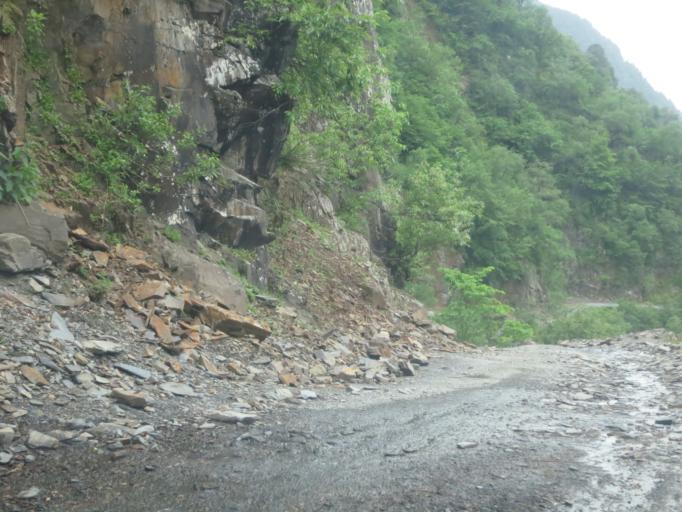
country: GE
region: Kakheti
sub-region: Telavi
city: Telavi
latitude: 42.2438
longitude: 45.4969
